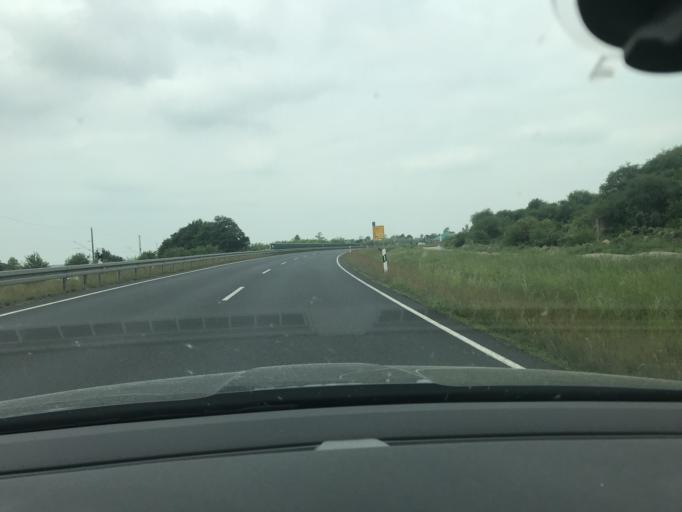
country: DE
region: Saxony
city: Grossenhain
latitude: 51.3021
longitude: 13.5569
